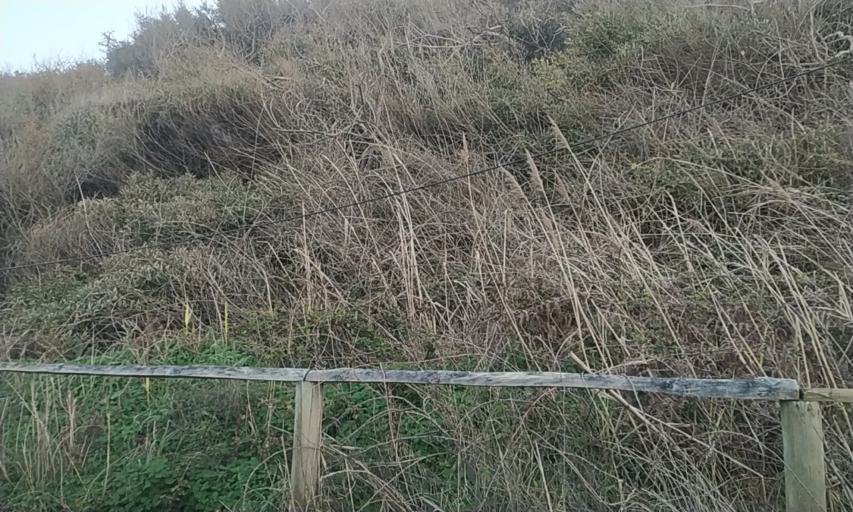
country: PT
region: Leiria
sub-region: Marinha Grande
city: Marinha Grande
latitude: 39.7746
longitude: -9.0224
